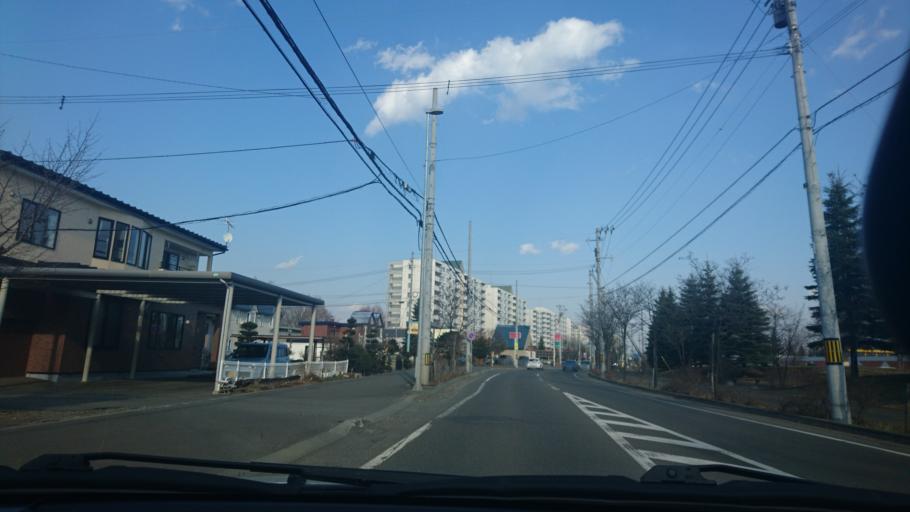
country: JP
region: Hokkaido
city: Obihiro
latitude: 42.9255
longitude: 143.1649
